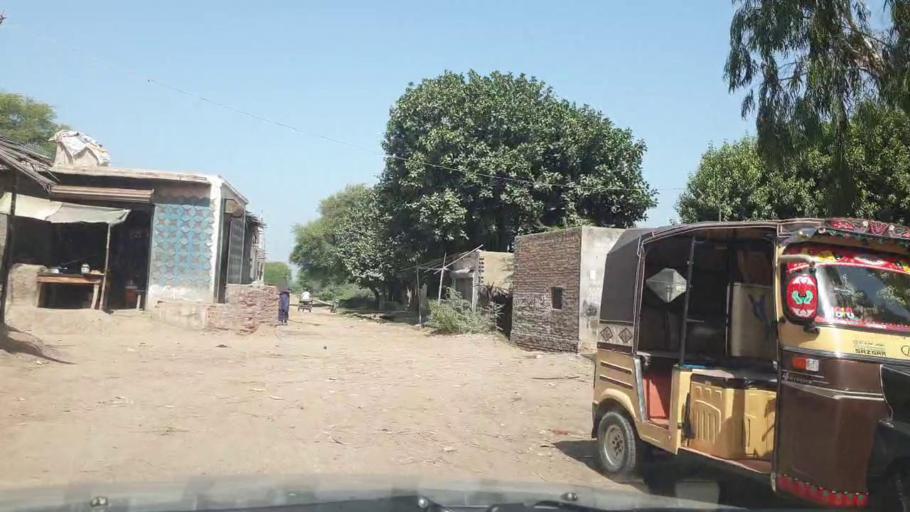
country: PK
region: Sindh
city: Tando Ghulam Ali
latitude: 25.1424
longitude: 68.7620
